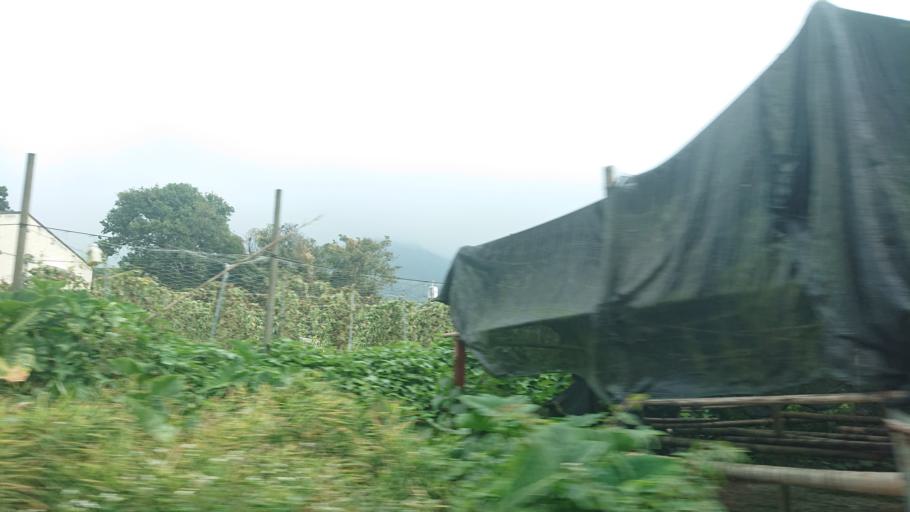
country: TW
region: Taiwan
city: Lugu
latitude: 23.6061
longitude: 120.7087
